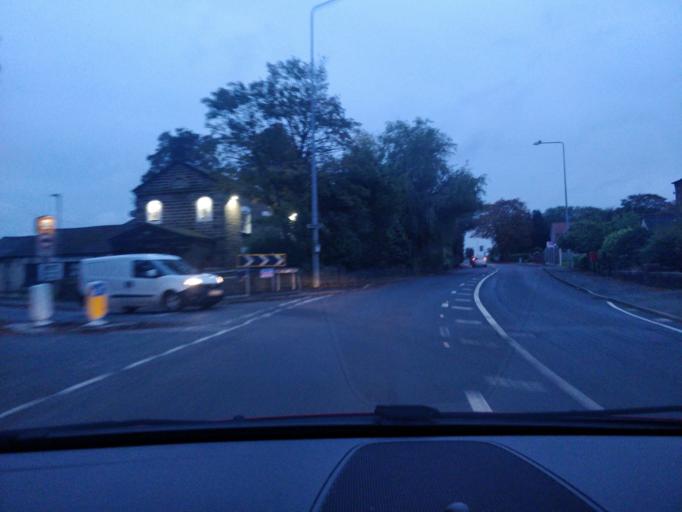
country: GB
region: England
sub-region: Lancashire
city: Ormskirk
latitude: 53.5969
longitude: -2.9229
